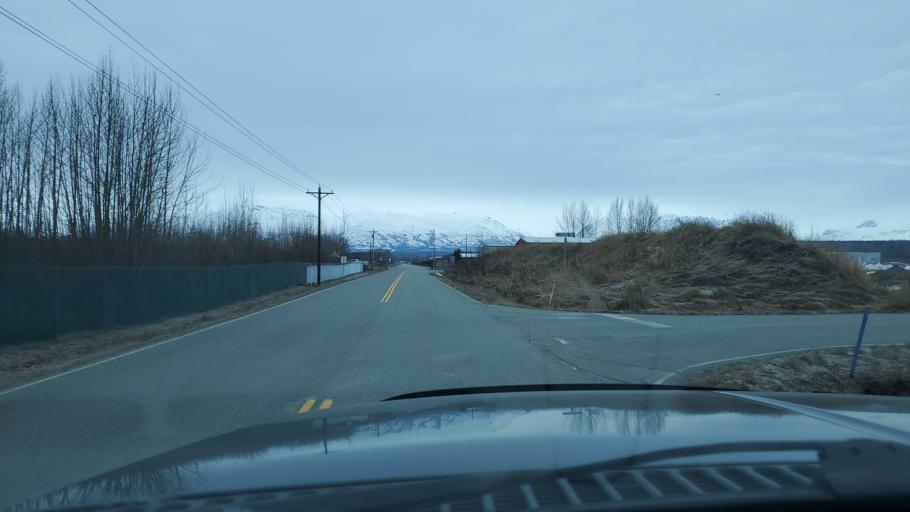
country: US
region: Alaska
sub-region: Matanuska-Susitna Borough
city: Palmer
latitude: 61.5978
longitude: -149.0952
